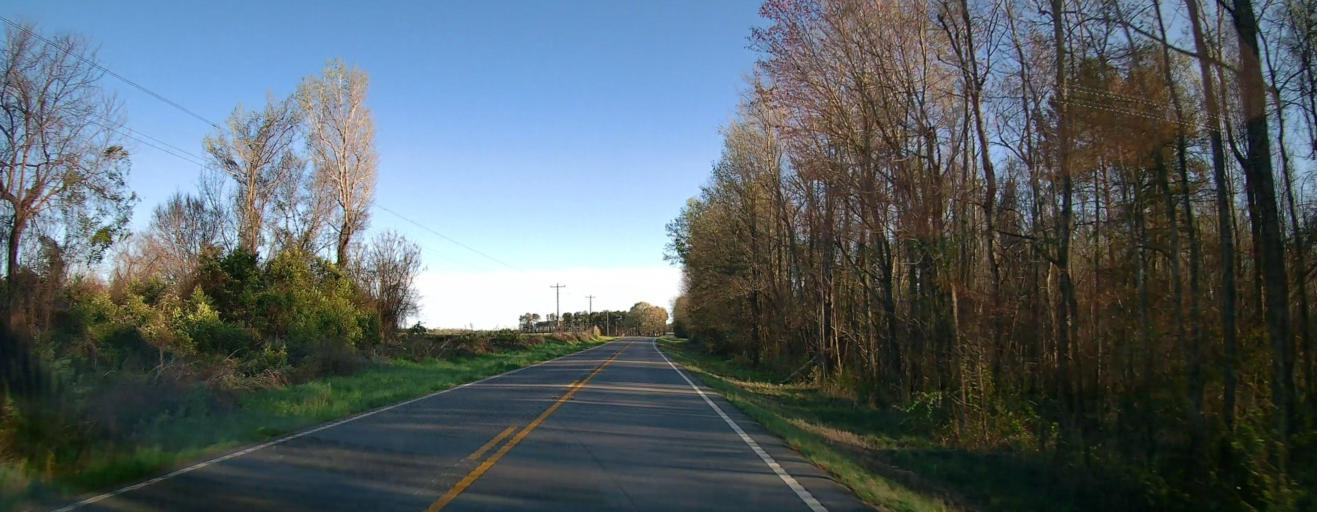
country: US
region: Georgia
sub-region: Pulaski County
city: Hawkinsville
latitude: 32.2203
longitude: -83.3876
